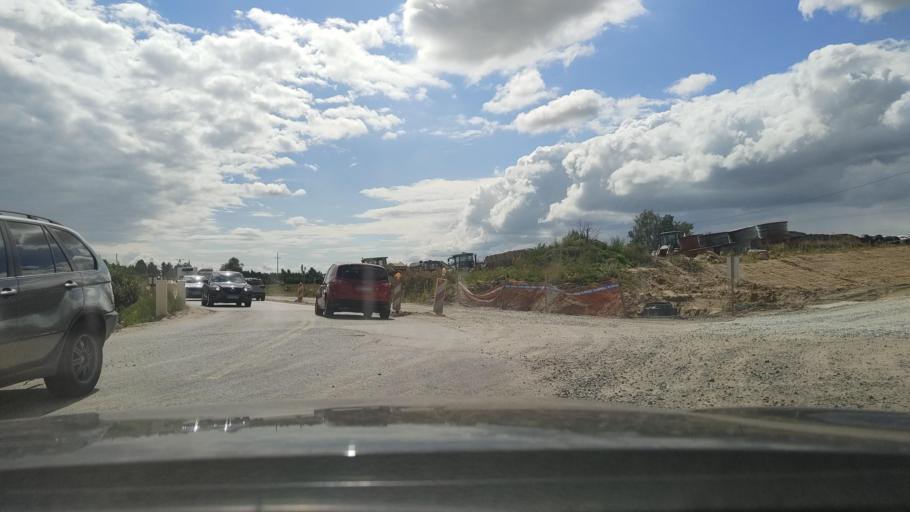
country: PL
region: Pomeranian Voivodeship
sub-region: Powiat wejherowski
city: Bojano
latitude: 54.4646
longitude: 18.3837
